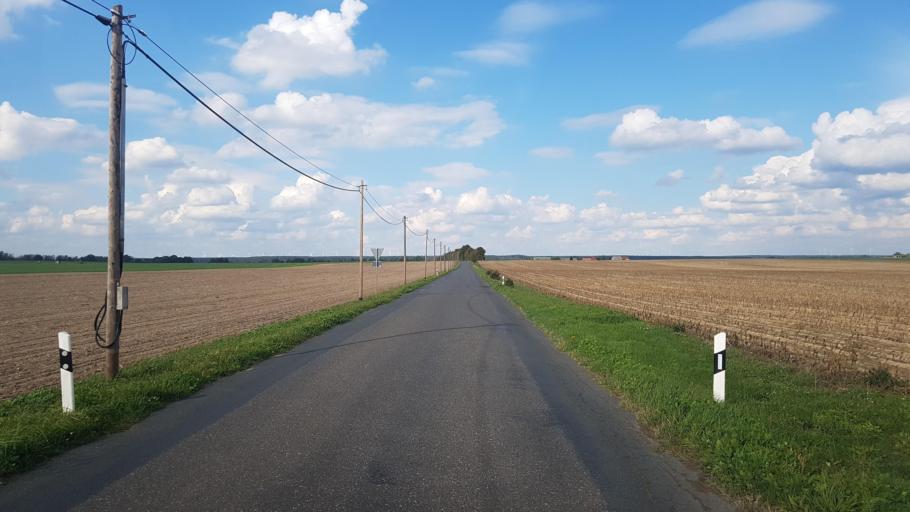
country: DE
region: Brandenburg
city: Dahme
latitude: 51.8708
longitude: 13.3836
